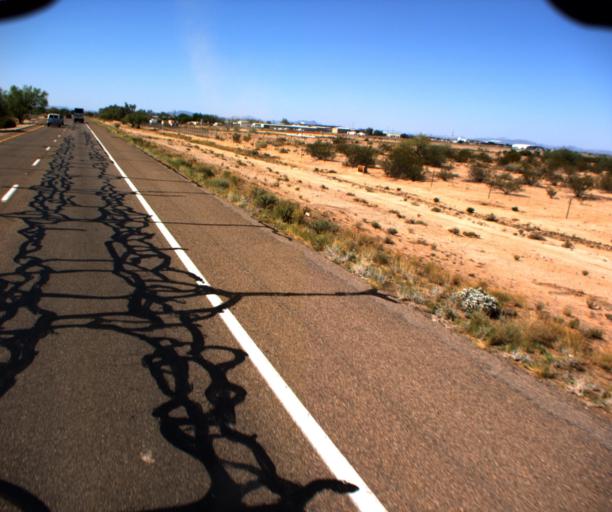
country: US
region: Arizona
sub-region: Pinal County
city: Casa Grande
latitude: 32.9614
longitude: -111.7569
